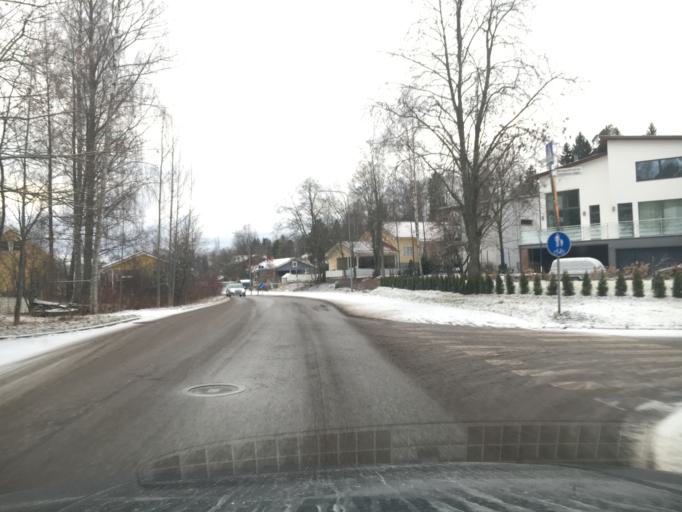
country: FI
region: Uusimaa
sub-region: Helsinki
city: Espoo
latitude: 60.1628
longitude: 24.6489
